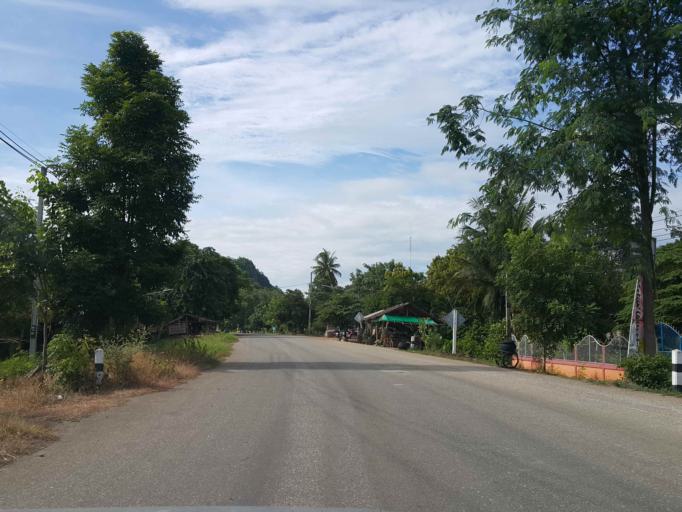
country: TH
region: Sukhothai
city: Thung Saliam
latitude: 17.2684
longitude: 99.5344
